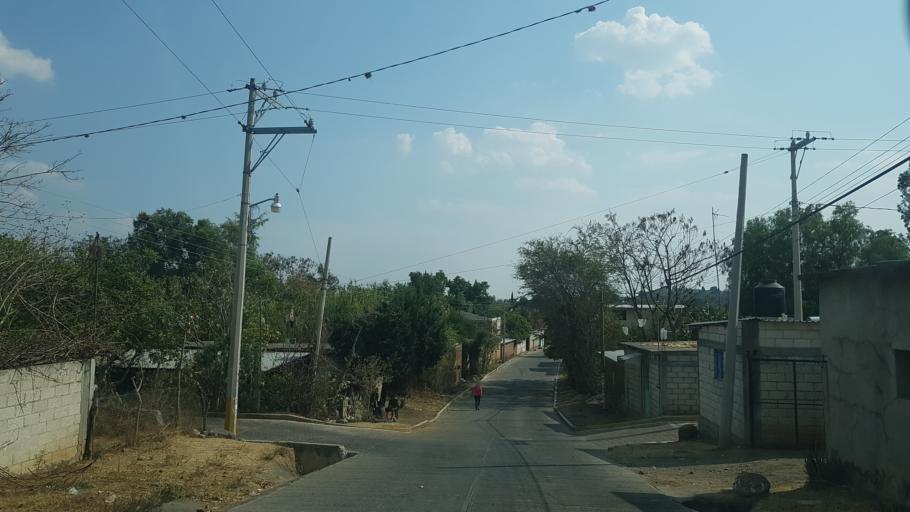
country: MX
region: Puebla
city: San Juan Amecac
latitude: 18.8233
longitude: -98.7045
